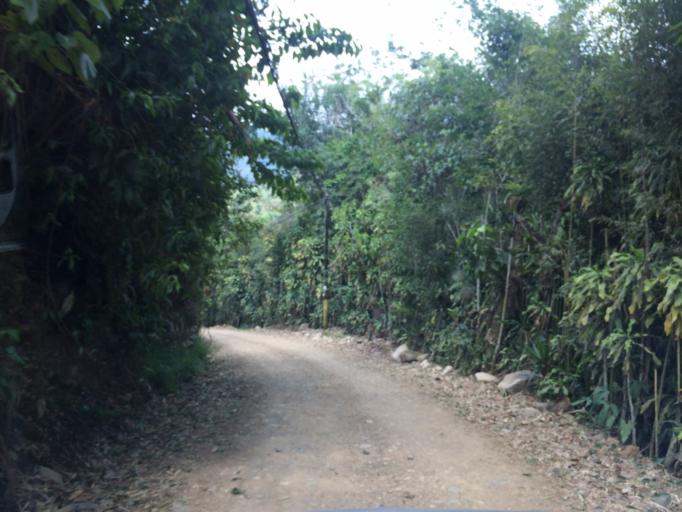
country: CR
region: San Jose
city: San Isidro
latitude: 9.4552
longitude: -83.6058
